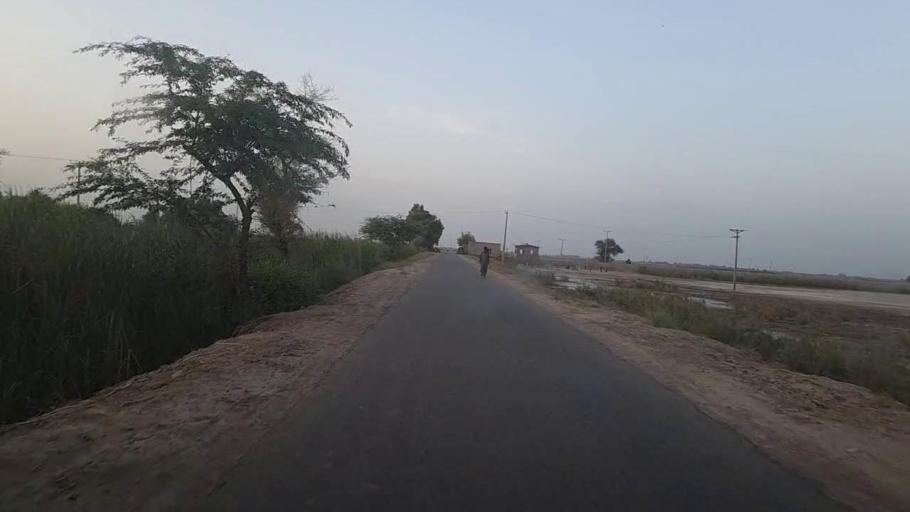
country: PK
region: Sindh
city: Radhan
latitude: 27.1424
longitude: 67.9351
